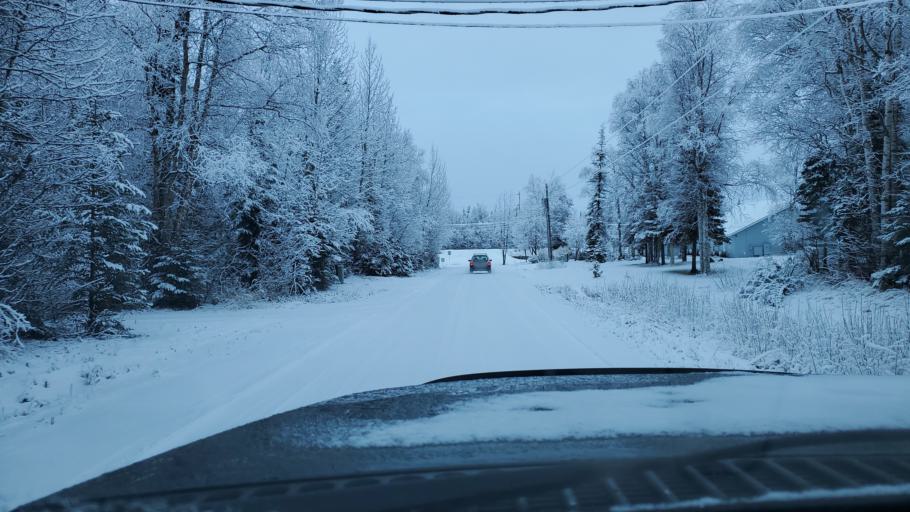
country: US
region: Alaska
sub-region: Matanuska-Susitna Borough
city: Wasilla
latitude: 61.5907
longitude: -149.4134
